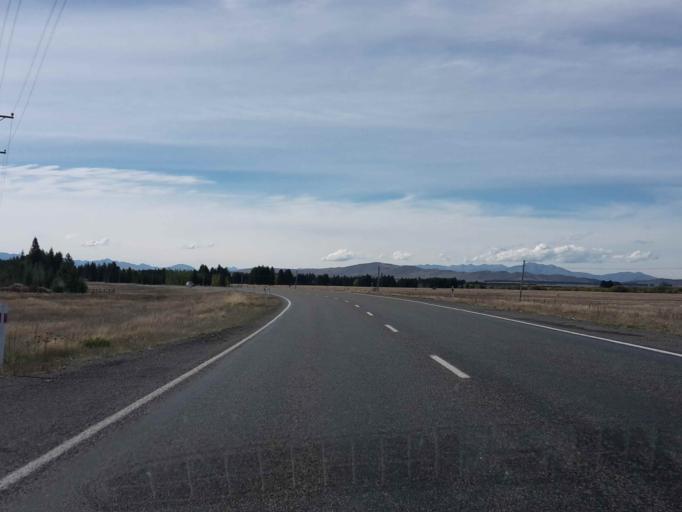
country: NZ
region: Canterbury
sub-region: Timaru District
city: Pleasant Point
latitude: -44.2763
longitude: 170.0972
